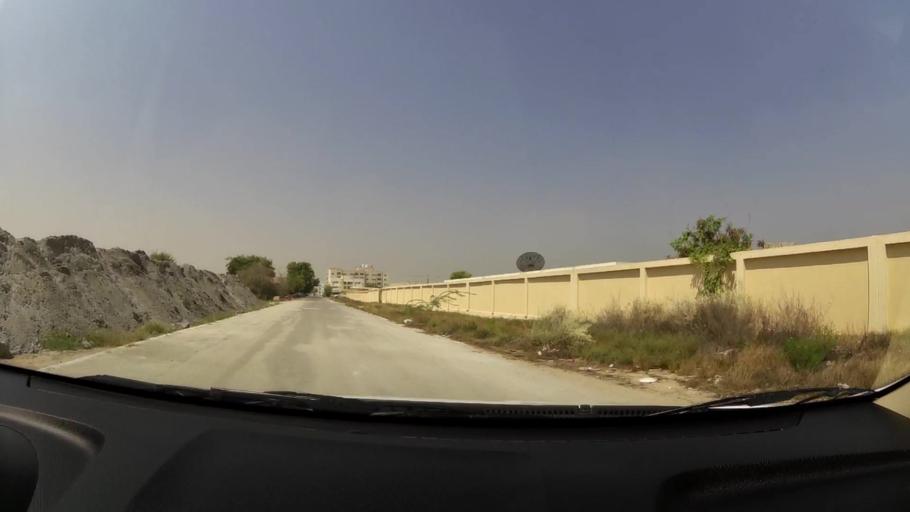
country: AE
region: Umm al Qaywayn
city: Umm al Qaywayn
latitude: 25.5720
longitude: 55.5596
